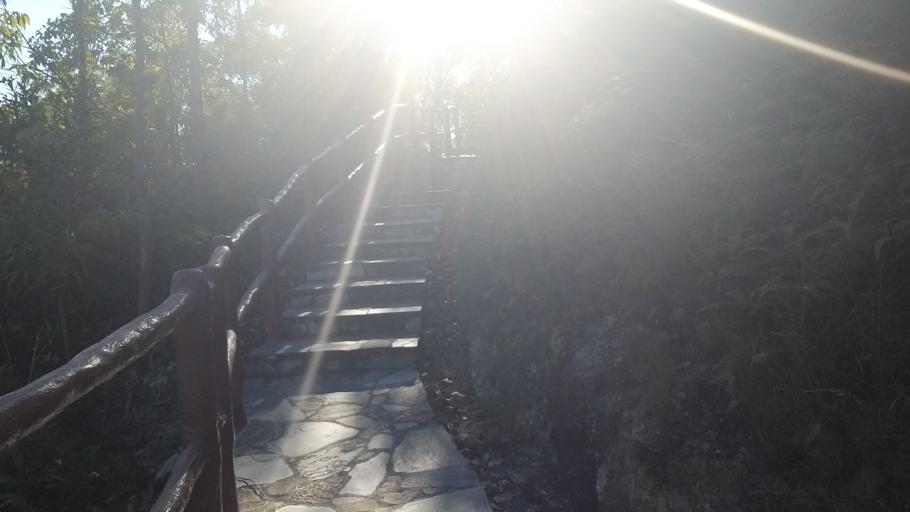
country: HK
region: Tuen Mun
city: Tuen Mun
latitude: 22.4006
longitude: 113.9878
